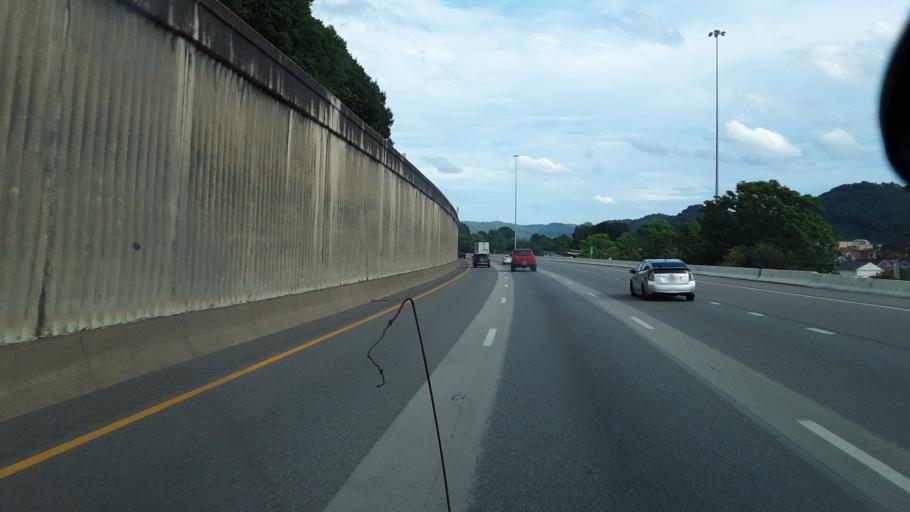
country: US
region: West Virginia
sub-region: Kanawha County
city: Charleston
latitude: 38.3385
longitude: -81.6111
